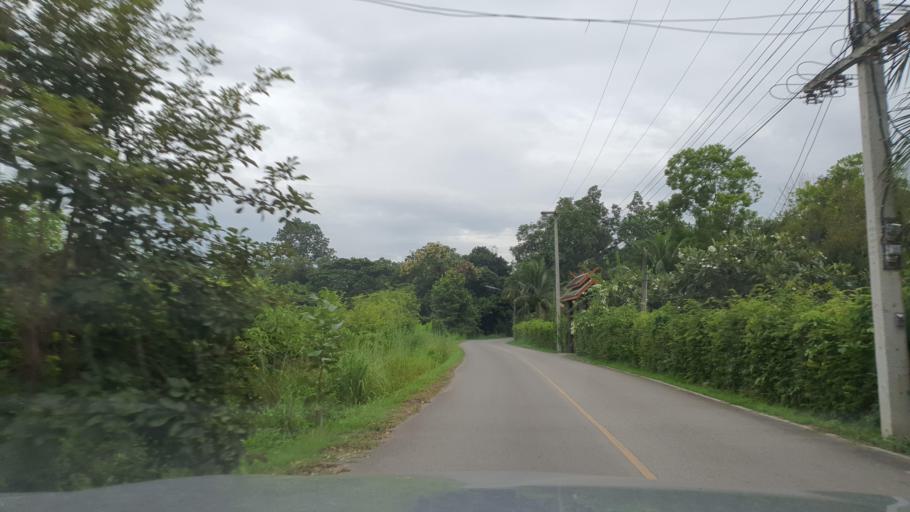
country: TH
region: Chiang Mai
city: San Sai
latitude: 18.9298
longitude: 98.9298
